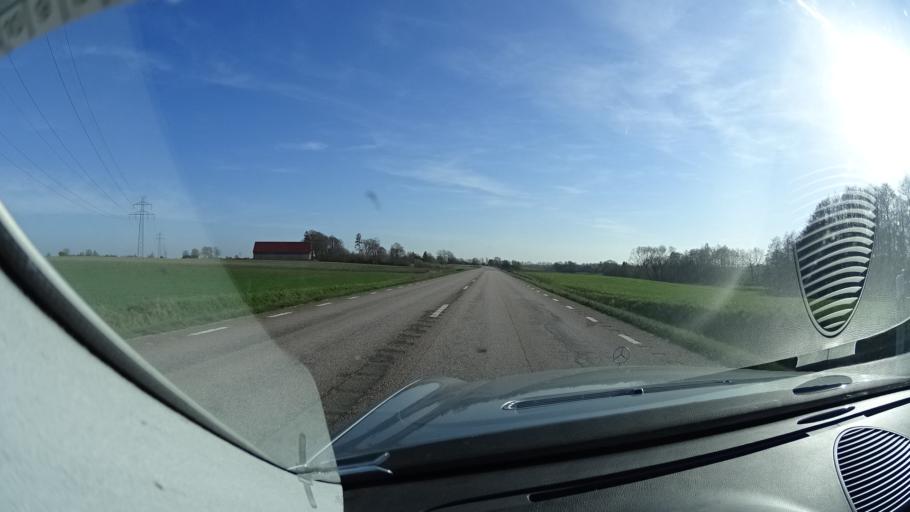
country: SE
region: Skane
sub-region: Bjuvs Kommun
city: Billesholm
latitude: 55.9865
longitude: 12.9387
